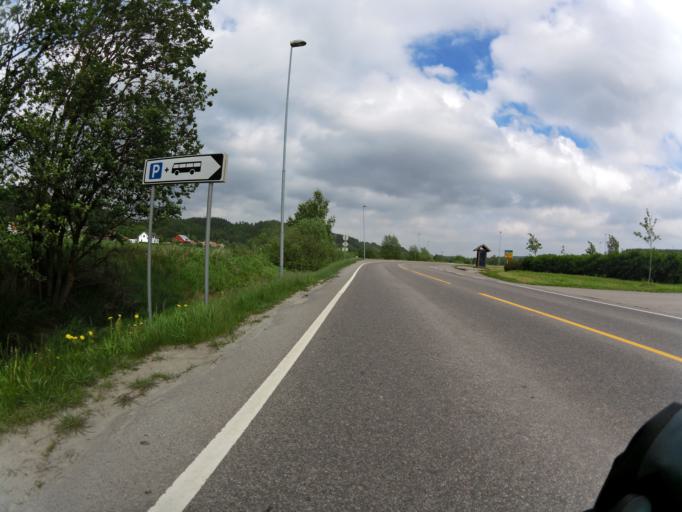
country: NO
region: Ostfold
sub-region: Rade
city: Karlshus
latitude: 59.3266
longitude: 10.9548
